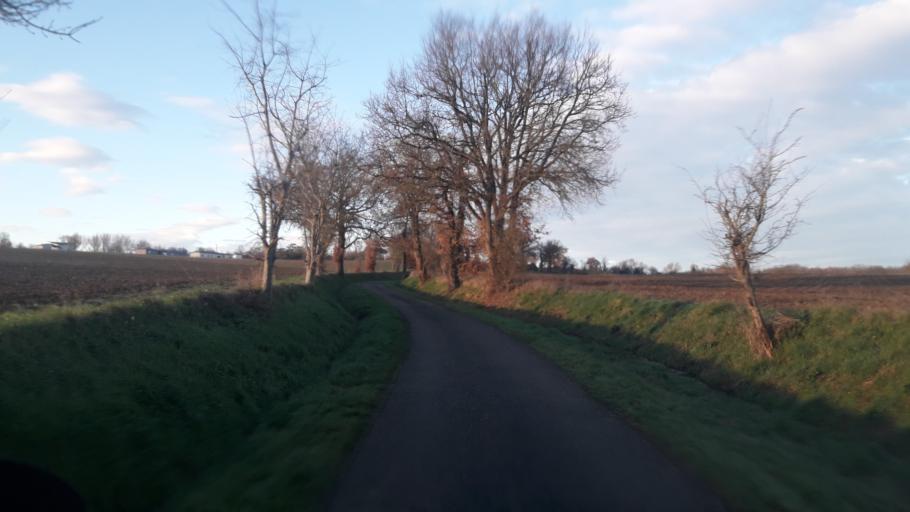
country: FR
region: Midi-Pyrenees
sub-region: Departement du Gers
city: Gimont
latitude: 43.7140
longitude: 0.9570
